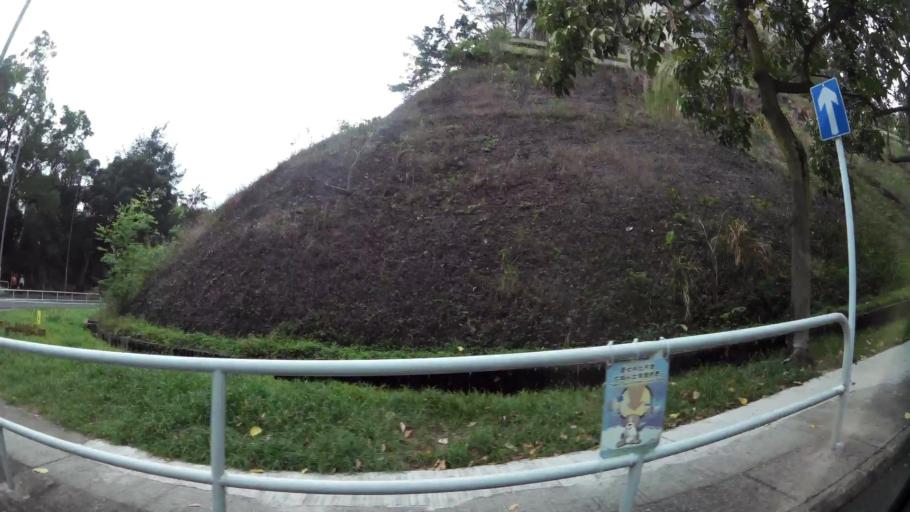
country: HK
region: Sha Tin
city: Sha Tin
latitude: 22.4011
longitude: 114.1975
